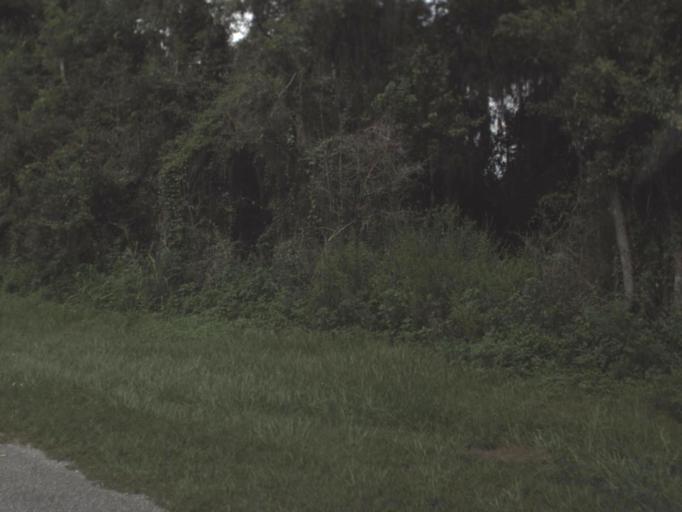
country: US
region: Florida
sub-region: Hernando County
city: Brooksville
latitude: 28.5777
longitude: -82.3754
